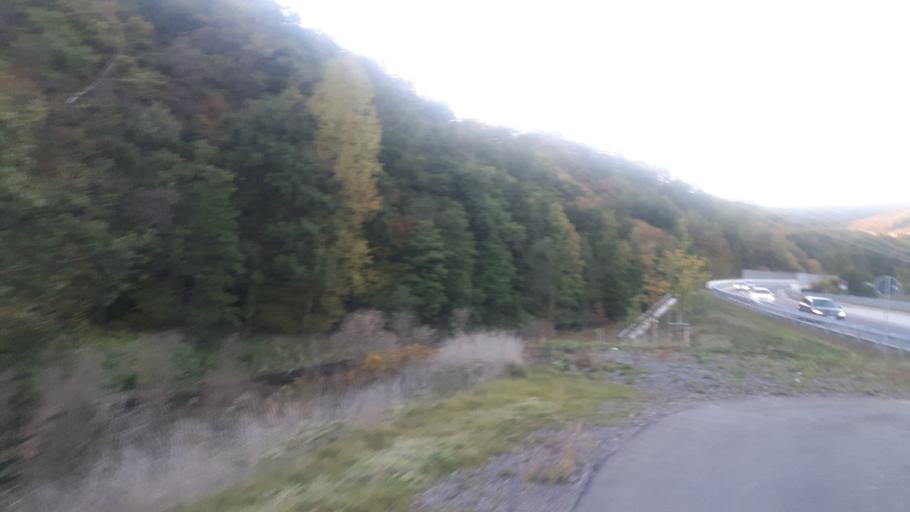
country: DE
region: North Rhine-Westphalia
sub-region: Regierungsbezirk Arnsberg
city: Neunkirchen
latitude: 50.8392
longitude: 7.9854
